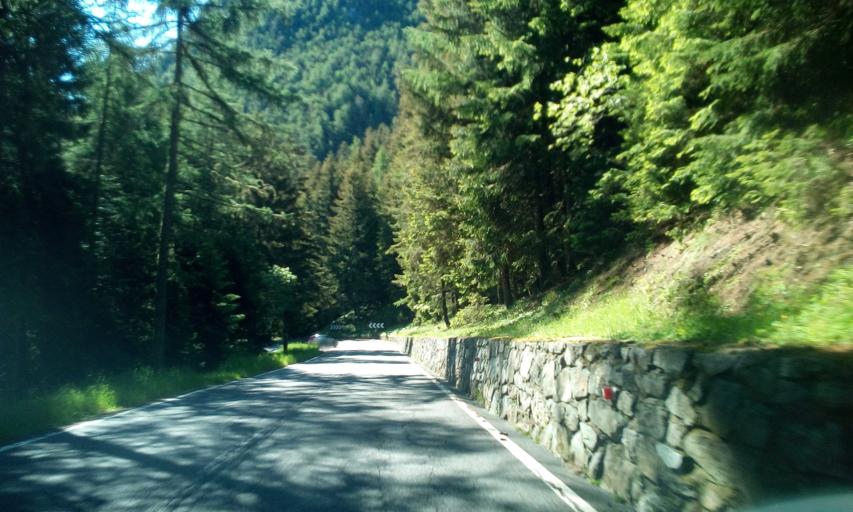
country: IT
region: Aosta Valley
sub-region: Valle d'Aosta
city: Brusson
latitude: 45.7536
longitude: 7.7095
